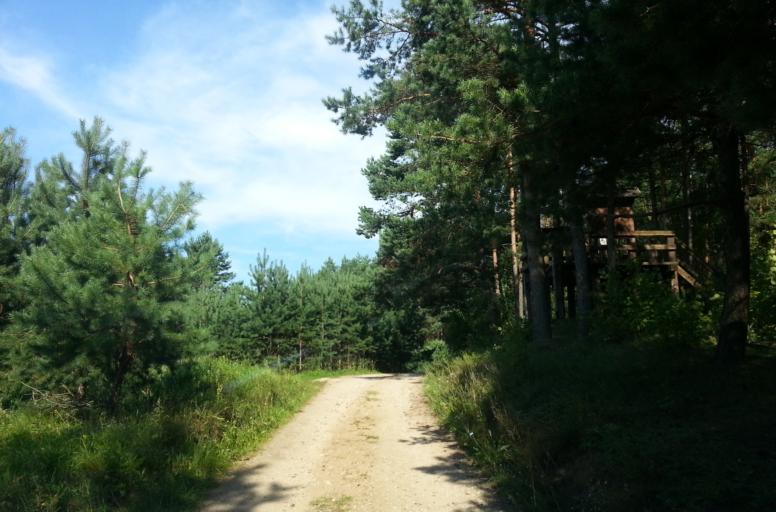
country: LT
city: Grigiskes
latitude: 54.7348
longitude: 25.0411
